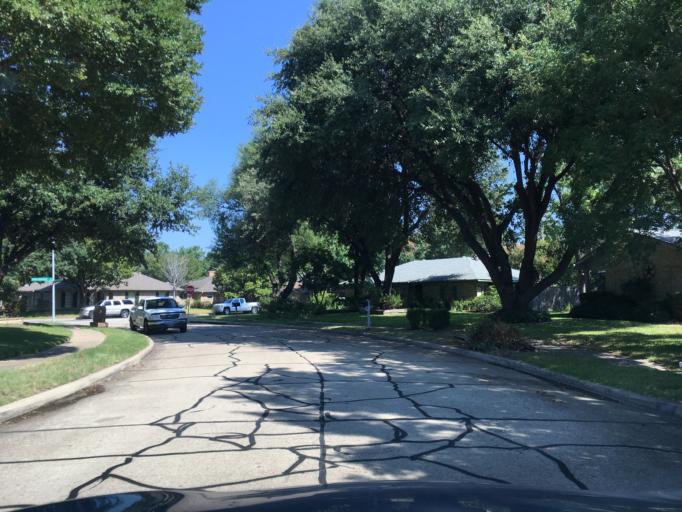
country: US
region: Texas
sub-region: Dallas County
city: Garland
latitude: 32.9377
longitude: -96.6366
